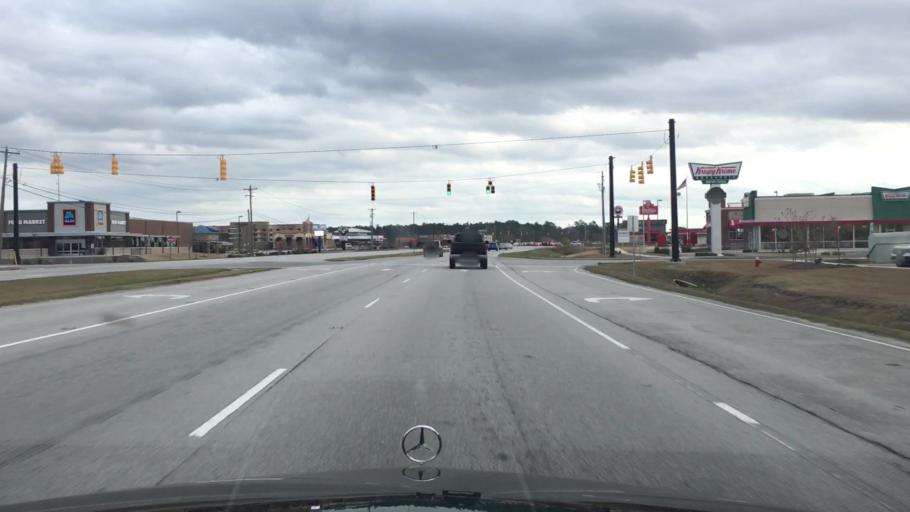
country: US
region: North Carolina
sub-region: Onslow County
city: Pumpkin Center
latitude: 34.7989
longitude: -77.4149
